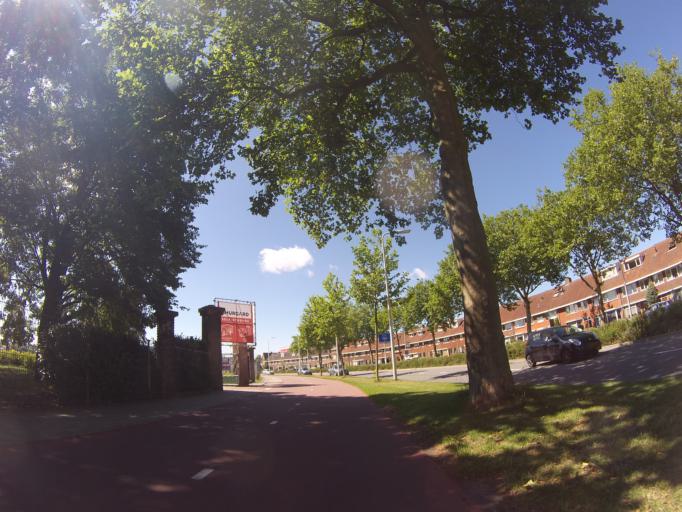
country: NL
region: Utrecht
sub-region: Gemeente Utrecht
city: Utrecht
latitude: 52.1018
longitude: 5.0875
